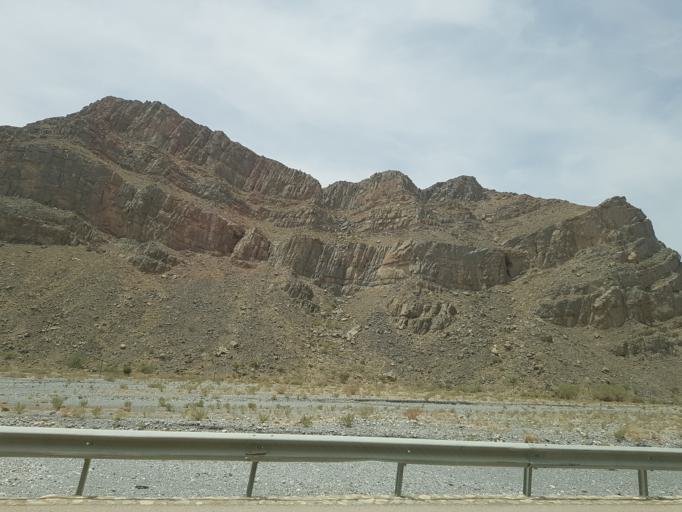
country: OM
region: Muhafazat ad Dakhiliyah
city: Izki
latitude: 22.9418
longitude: 57.6735
